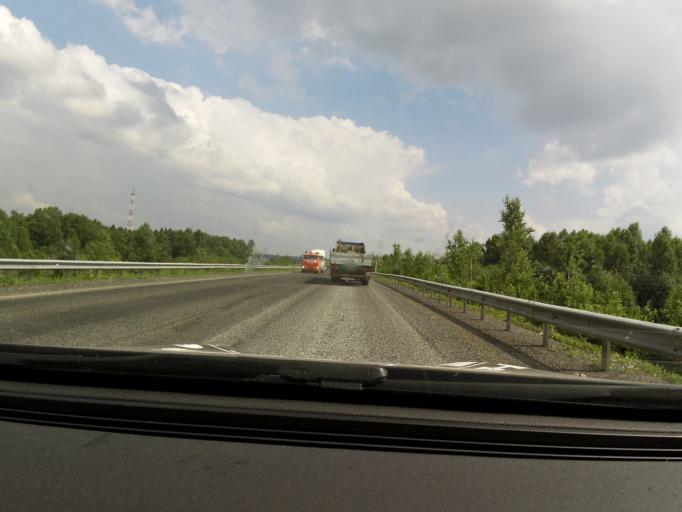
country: RU
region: Sverdlovsk
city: Ufimskiy
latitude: 56.7642
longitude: 58.1404
